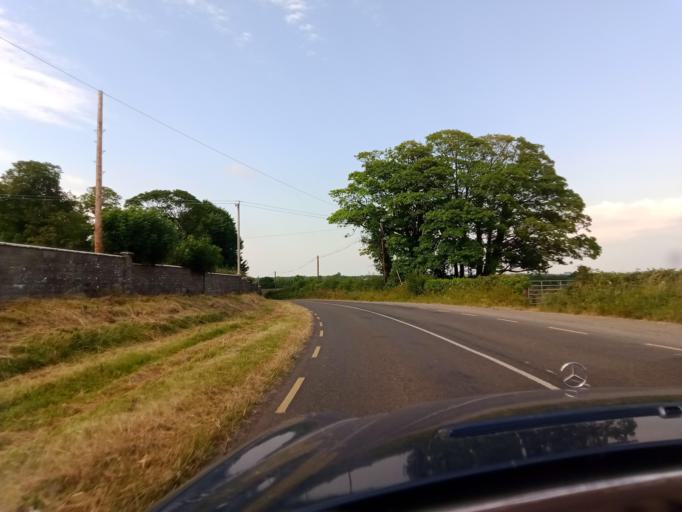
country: IE
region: Leinster
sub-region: Kilkenny
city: Callan
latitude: 52.4856
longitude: -7.3237
